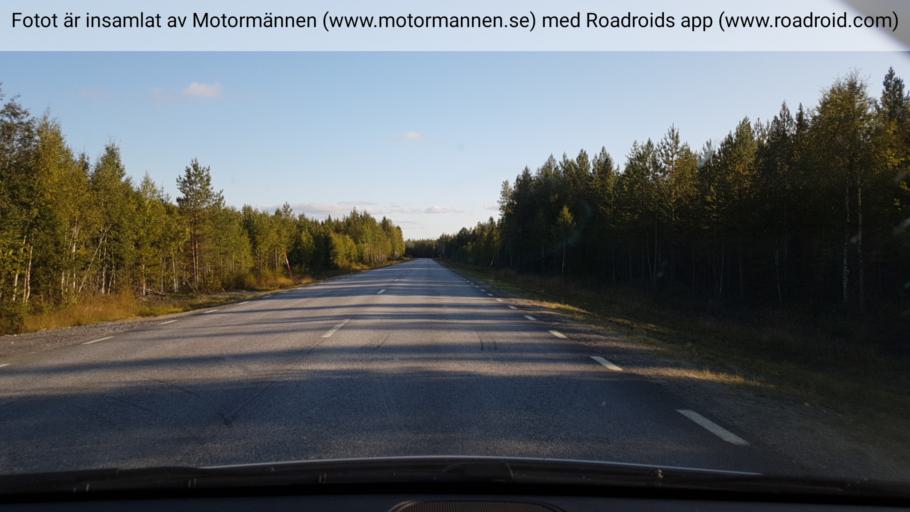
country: SE
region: Vaesterbotten
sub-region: Vannas Kommun
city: Vaennaes
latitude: 63.9535
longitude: 19.7564
